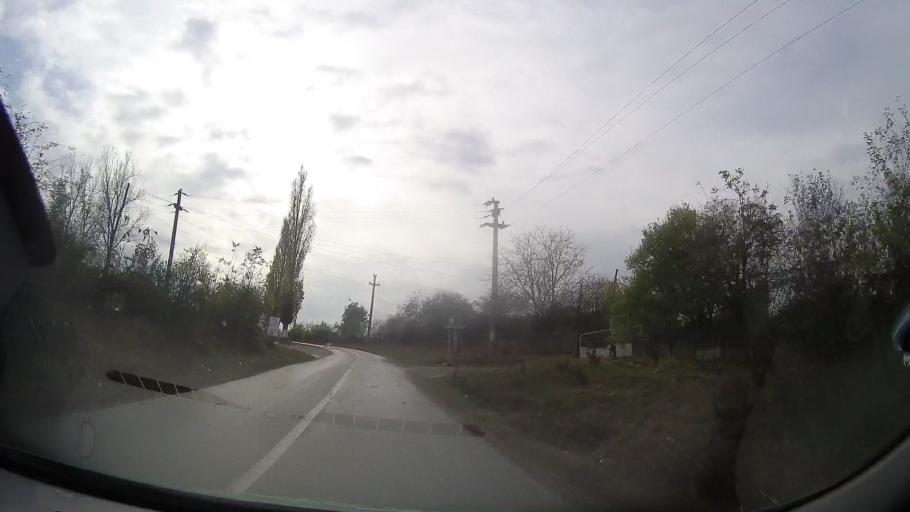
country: RO
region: Ialomita
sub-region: Comuna Maia
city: Maia
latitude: 44.7278
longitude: 26.3935
